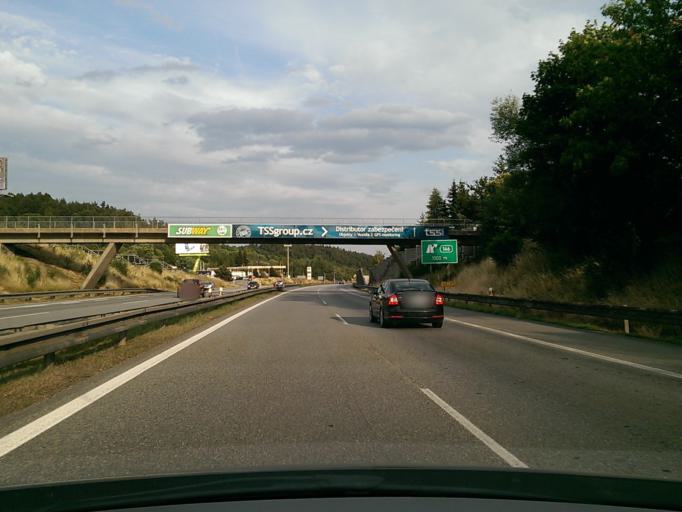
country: CZ
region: Vysocina
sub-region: Okres Zd'ar nad Sazavou
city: Velke Mezirici
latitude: 49.3554
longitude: 16.0286
